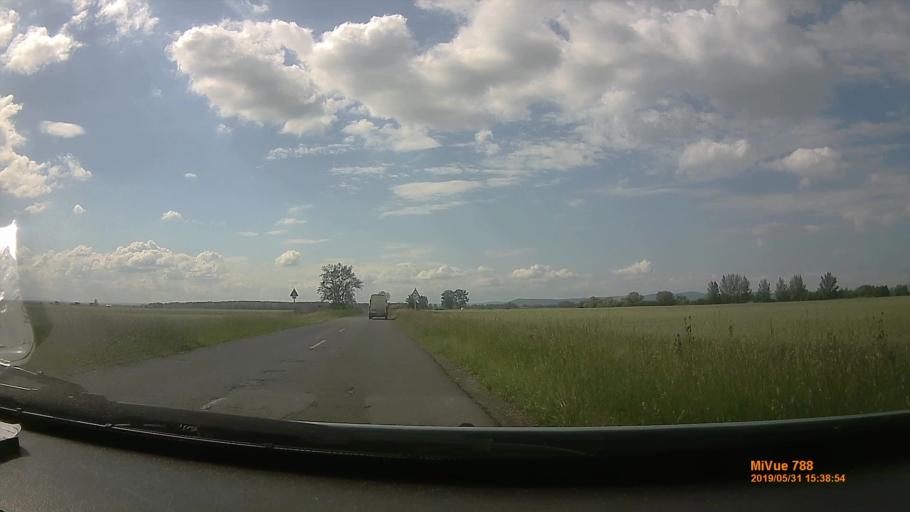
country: HU
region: Borsod-Abauj-Zemplen
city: Prugy
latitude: 48.1045
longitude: 21.2329
